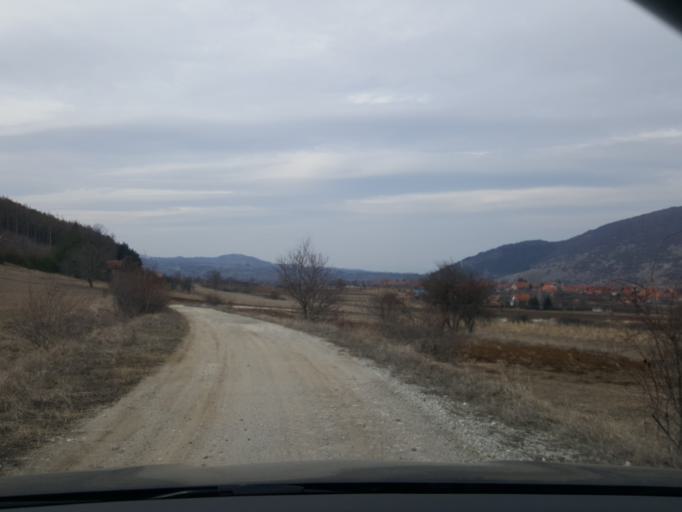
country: RS
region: Central Serbia
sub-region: Pirotski Okrug
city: Dimitrovgrad
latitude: 43.0081
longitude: 22.7480
